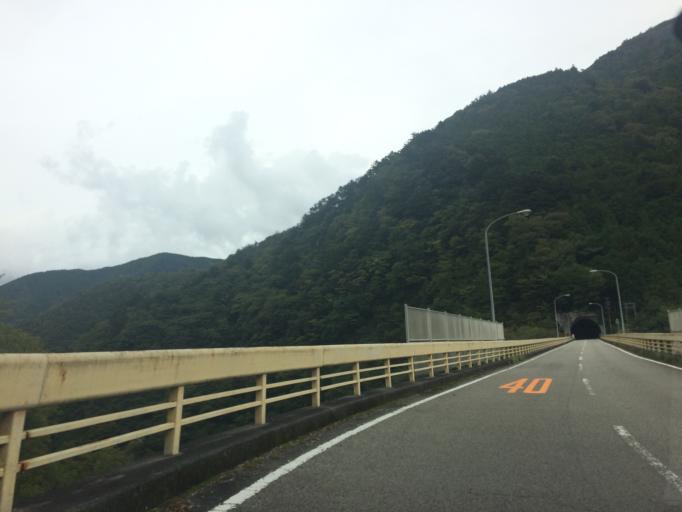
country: JP
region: Shizuoka
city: Shizuoka-shi
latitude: 35.1551
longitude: 138.1438
